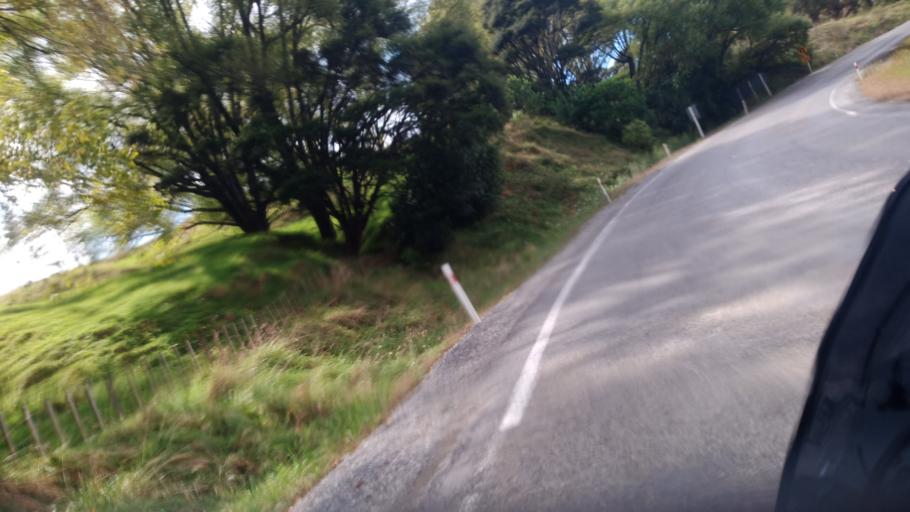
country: NZ
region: Gisborne
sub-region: Gisborne District
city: Gisborne
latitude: -38.1569
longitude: 178.2845
